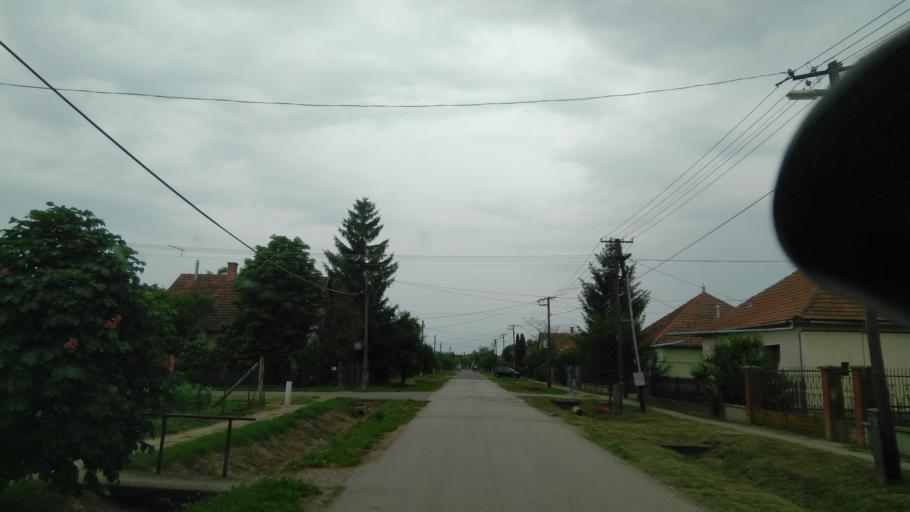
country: HU
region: Bekes
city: Doboz
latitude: 46.7340
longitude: 21.2521
